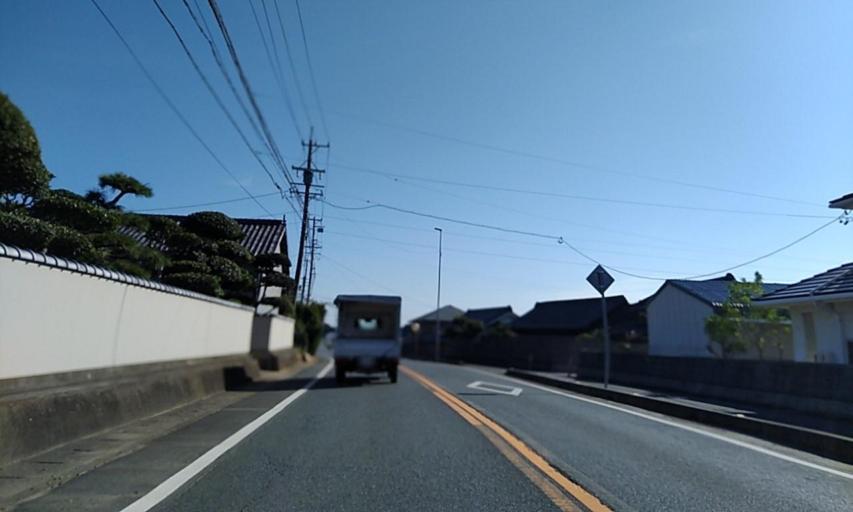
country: JP
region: Aichi
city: Tahara
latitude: 34.5919
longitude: 137.1391
